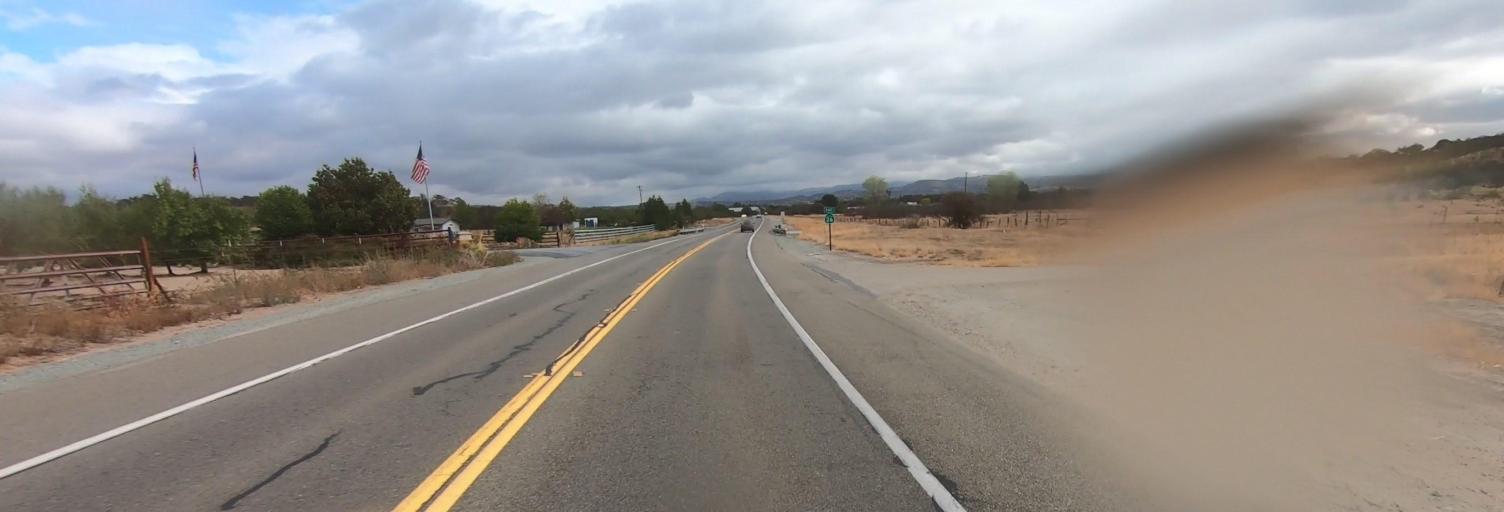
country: US
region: California
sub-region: Calaveras County
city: Rancho Calaveras
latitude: 38.0988
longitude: -120.9365
